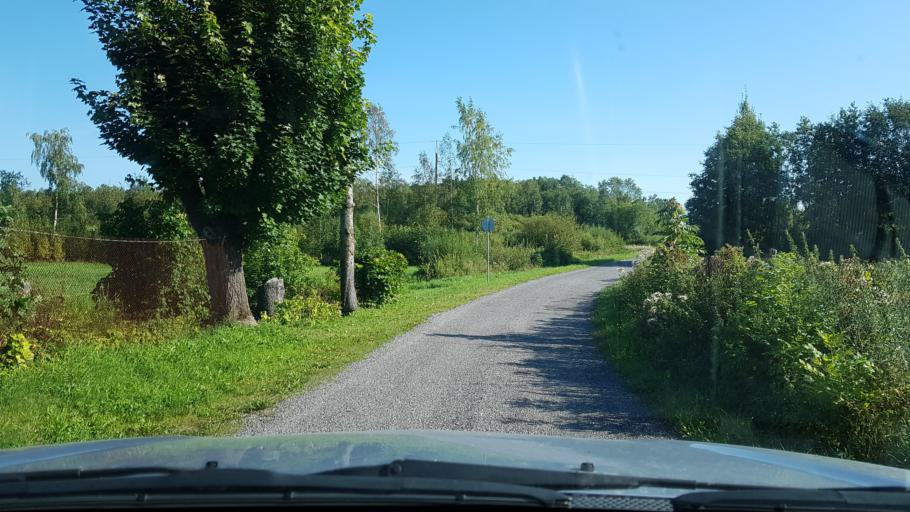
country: EE
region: Ida-Virumaa
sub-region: Narva-Joesuu linn
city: Narva-Joesuu
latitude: 59.4024
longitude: 28.0031
